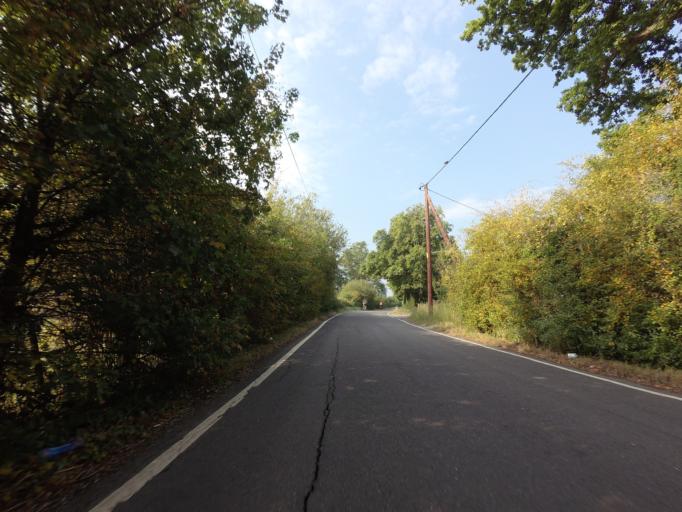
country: GB
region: England
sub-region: Kent
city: Tenterden
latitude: 51.1166
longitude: 0.6867
